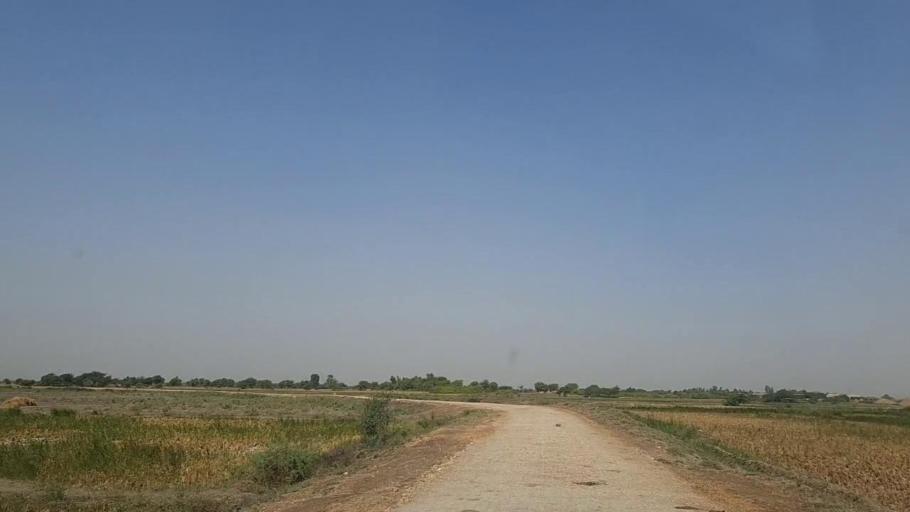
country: PK
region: Sindh
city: Daro Mehar
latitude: 24.7516
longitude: 68.1398
